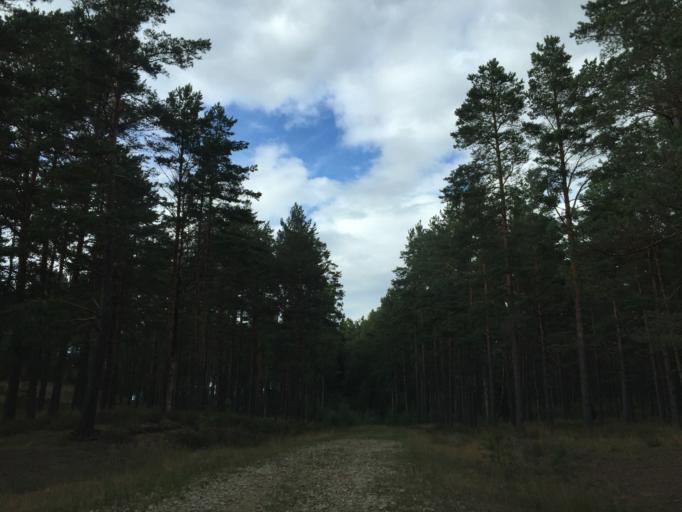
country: LV
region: Saulkrastu
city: Saulkrasti
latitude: 57.1743
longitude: 24.3754
